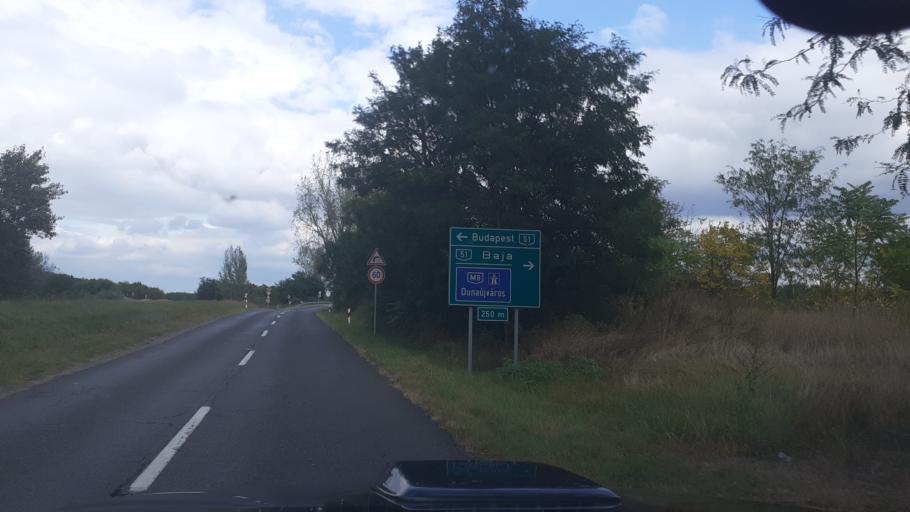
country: HU
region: Bacs-Kiskun
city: Dunavecse
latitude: 46.9333
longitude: 18.9819
